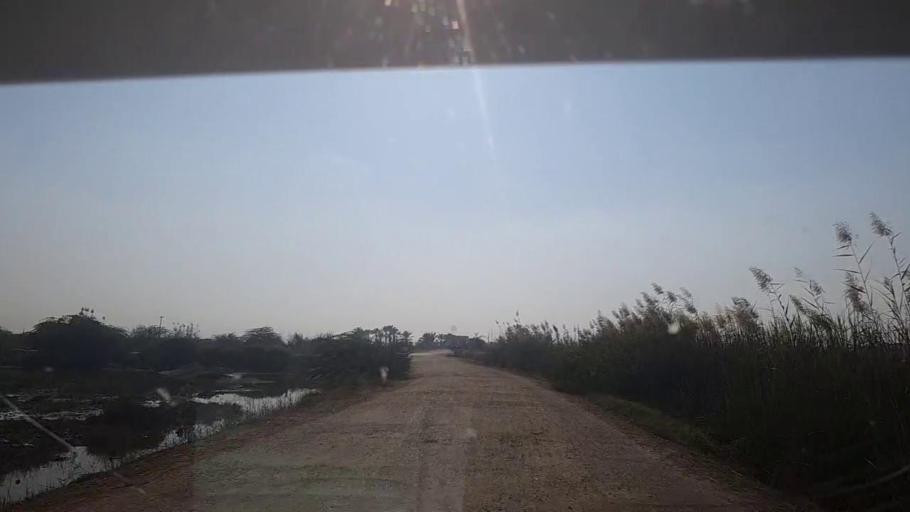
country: PK
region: Sindh
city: Gambat
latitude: 27.3636
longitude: 68.5575
